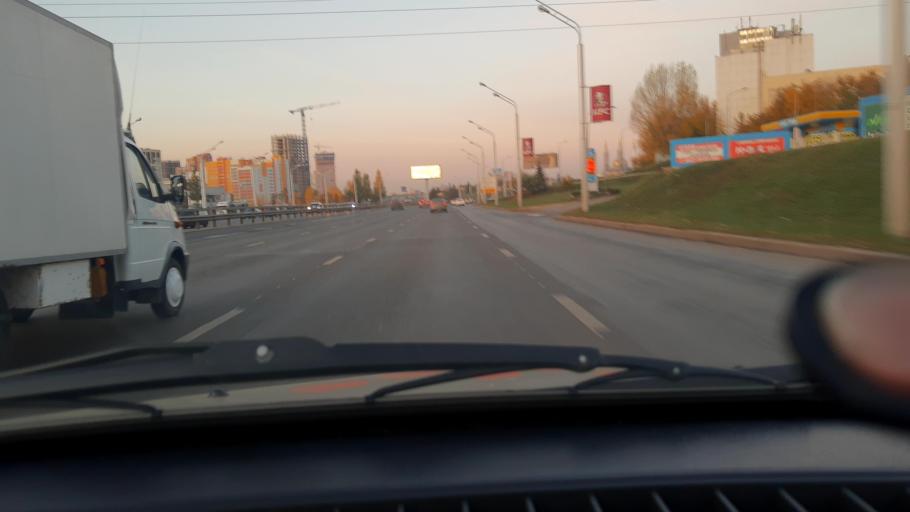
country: RU
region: Bashkortostan
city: Ufa
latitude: 54.7227
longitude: 55.9835
